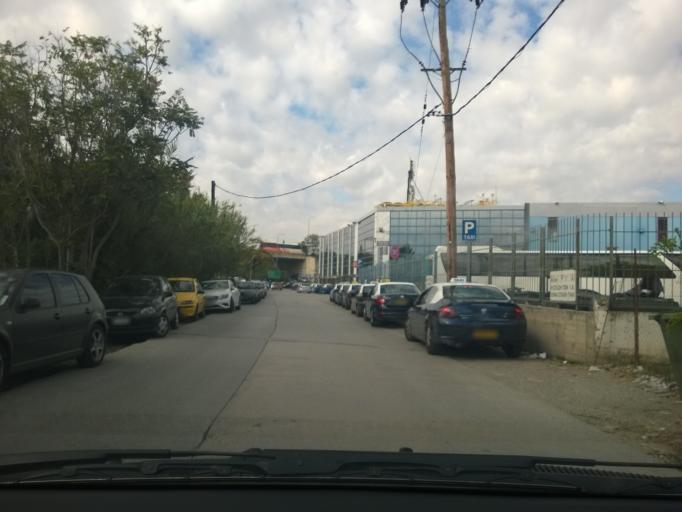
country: GR
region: Central Macedonia
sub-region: Nomos Thessalonikis
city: Menemeni
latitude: 40.6537
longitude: 22.9033
